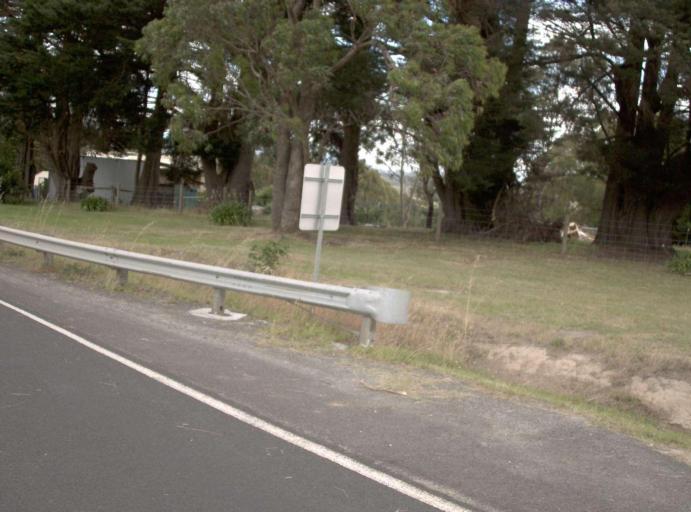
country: AU
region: Victoria
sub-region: Latrobe
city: Moe
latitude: -38.1144
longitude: 146.2521
